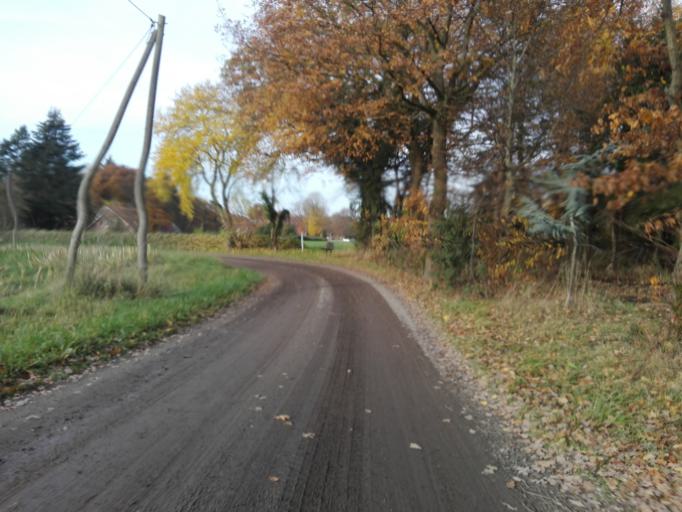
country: DE
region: Lower Saxony
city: Wiefelstede
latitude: 53.2783
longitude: 8.1482
